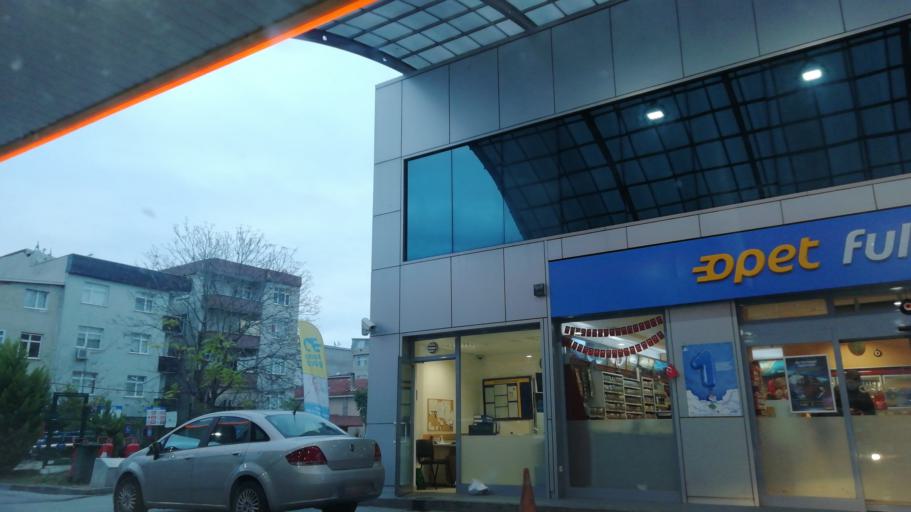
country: TR
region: Istanbul
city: Bahcelievler
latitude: 41.0117
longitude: 28.8284
